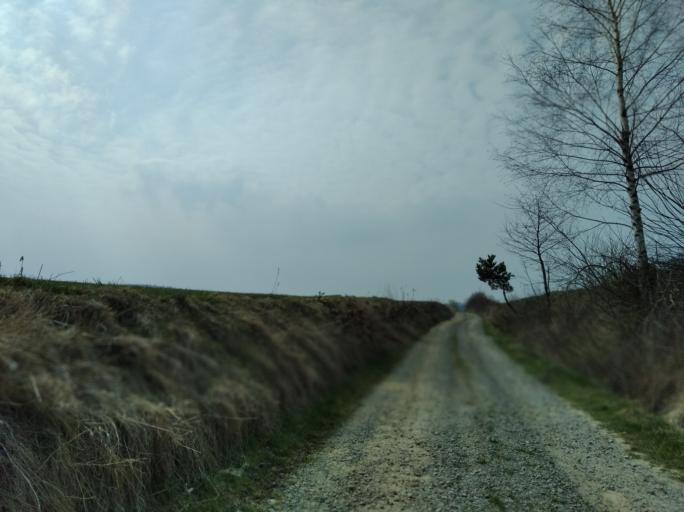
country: PL
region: Subcarpathian Voivodeship
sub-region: Powiat strzyzowski
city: Strzyzow
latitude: 49.7958
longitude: 21.8160
